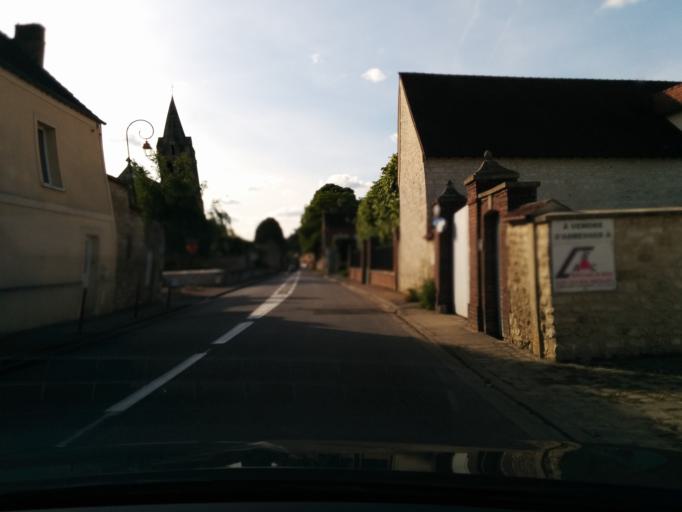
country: FR
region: Haute-Normandie
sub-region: Departement de l'Eure
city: Courcelles-sur-Seine
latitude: 49.1689
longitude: 1.4073
